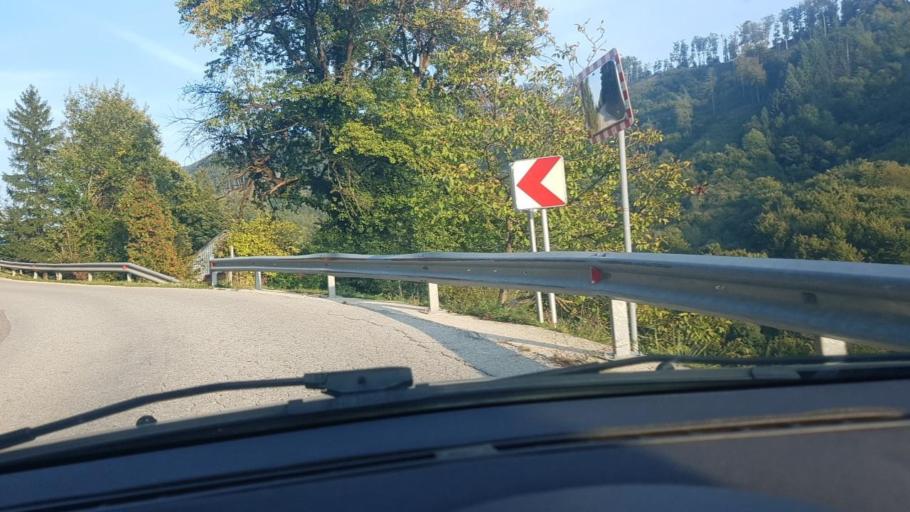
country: SI
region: Rogatec
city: Rogatec
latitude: 46.2647
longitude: 15.7071
